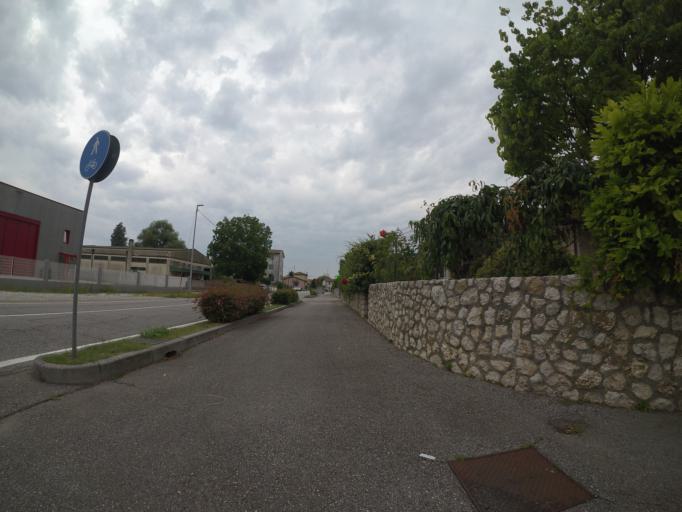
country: IT
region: Friuli Venezia Giulia
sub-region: Provincia di Udine
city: Varmo
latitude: 45.8852
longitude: 12.9940
